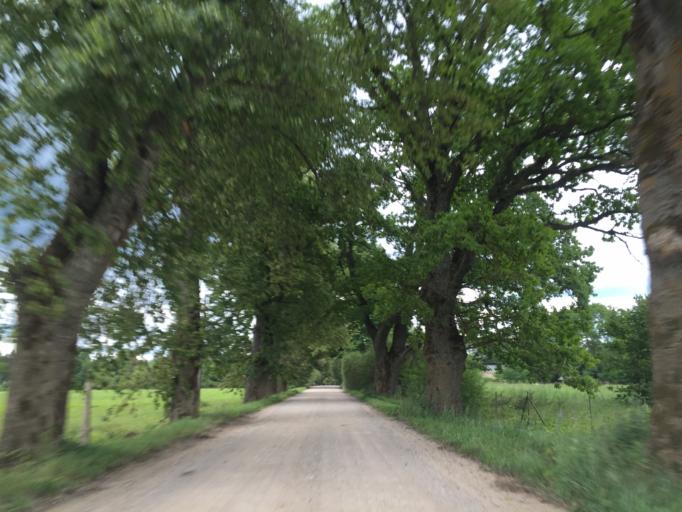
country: LV
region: Malpils
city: Malpils
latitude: 56.9270
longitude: 25.0092
